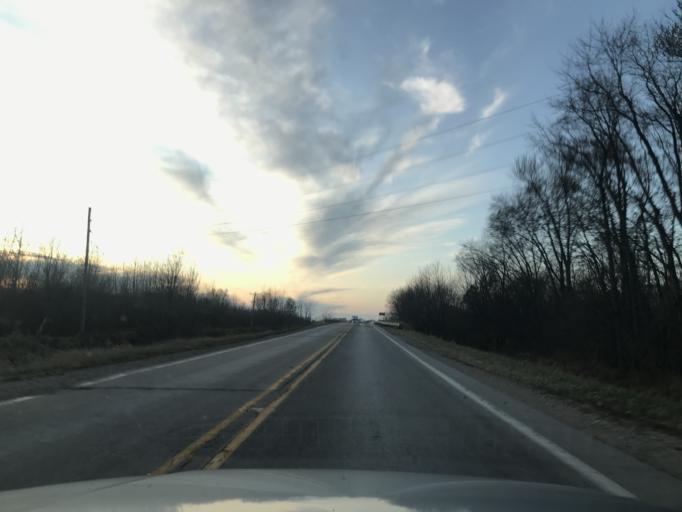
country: US
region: Illinois
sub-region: Henderson County
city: Oquawka
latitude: 41.0189
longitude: -90.8074
